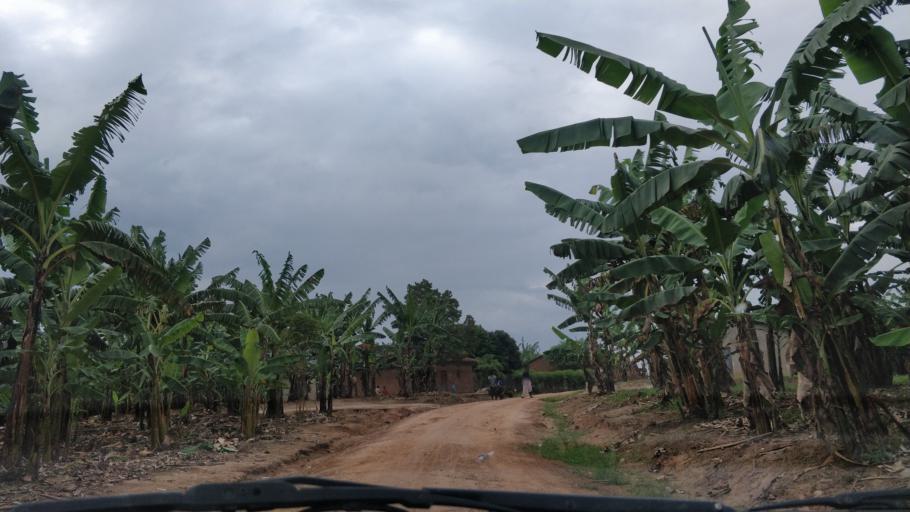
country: UG
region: Western Region
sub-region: Sheema District
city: Kibingo
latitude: -0.6406
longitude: 30.4897
